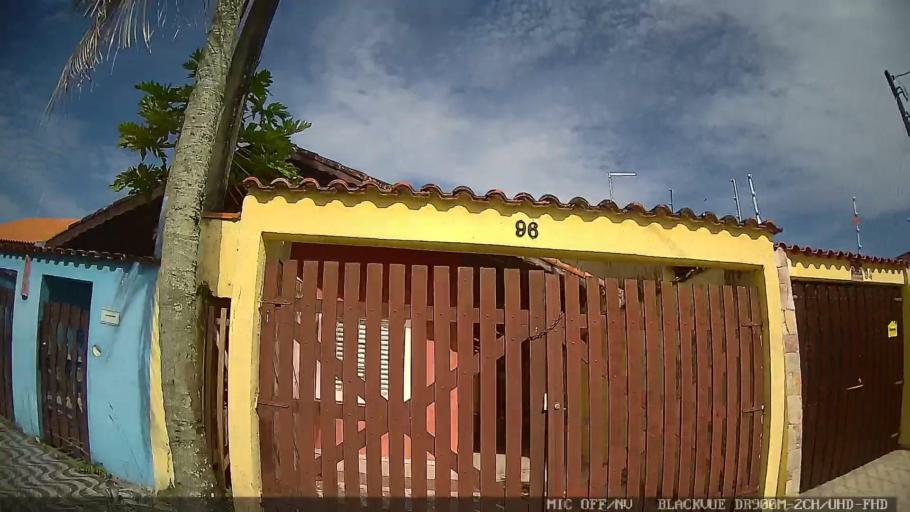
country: BR
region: Sao Paulo
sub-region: Itanhaem
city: Itanhaem
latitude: -24.1631
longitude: -46.7595
